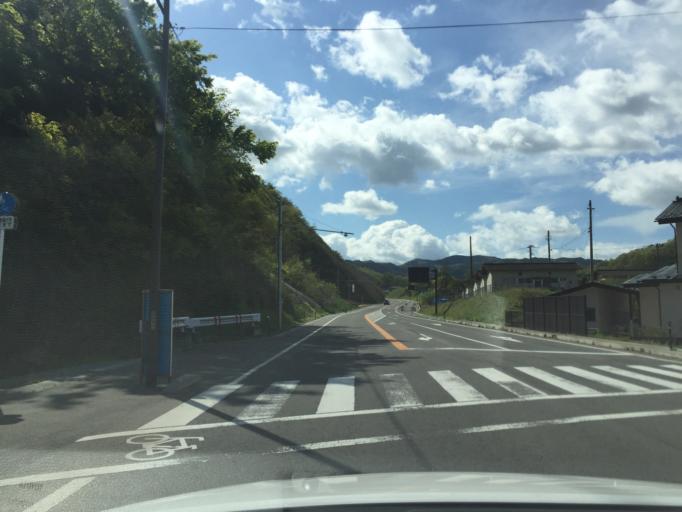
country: JP
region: Fukushima
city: Fukushima-shi
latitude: 37.6560
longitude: 140.6075
